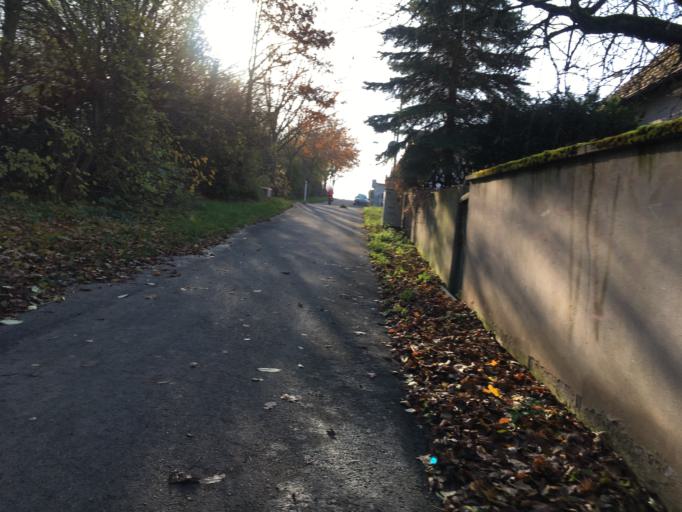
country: DE
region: Rheinland-Pfalz
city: Mainz
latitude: 49.9702
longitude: 8.2935
